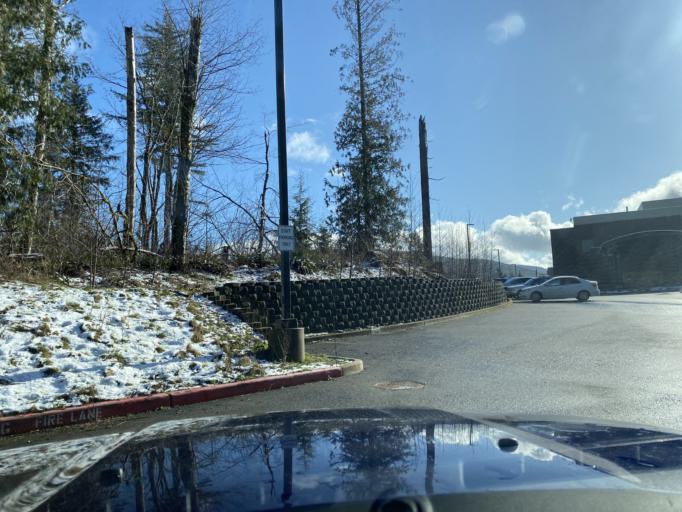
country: US
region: Washington
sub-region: King County
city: Fall City
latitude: 47.5137
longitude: -121.8859
